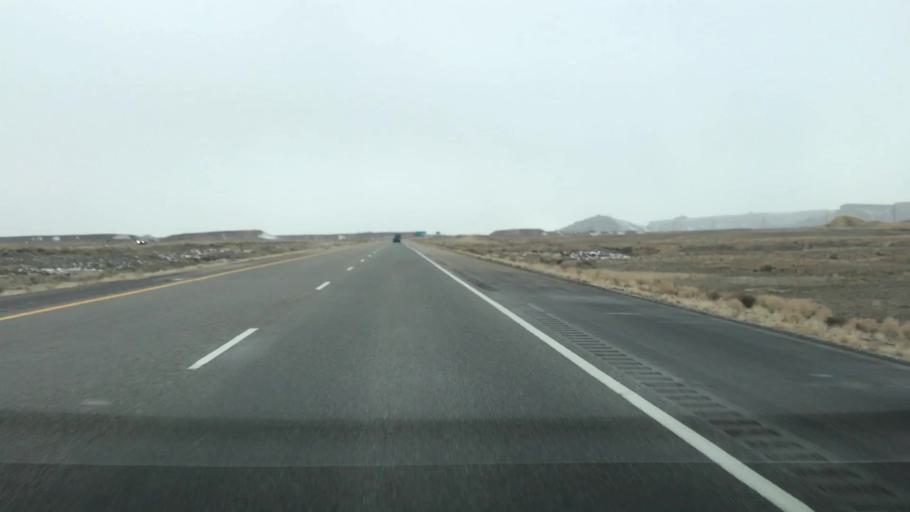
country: US
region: Utah
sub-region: Grand County
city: Moab
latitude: 38.9476
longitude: -109.7922
